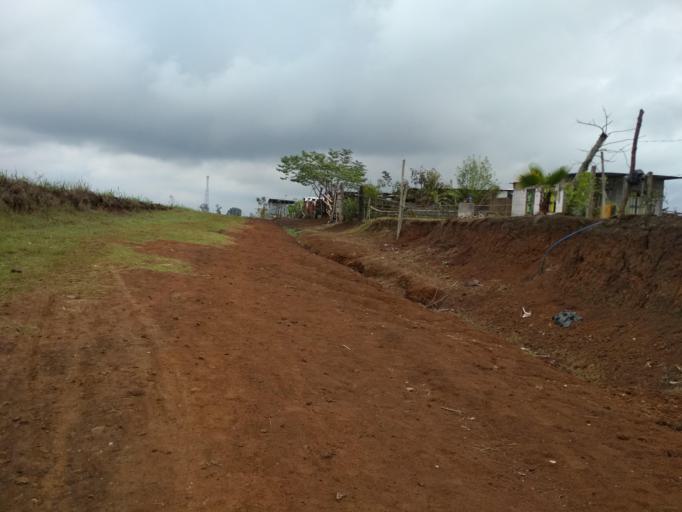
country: MX
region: Veracruz
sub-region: Cordoba
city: San Jose de Tapia
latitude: 18.8499
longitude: -96.9644
